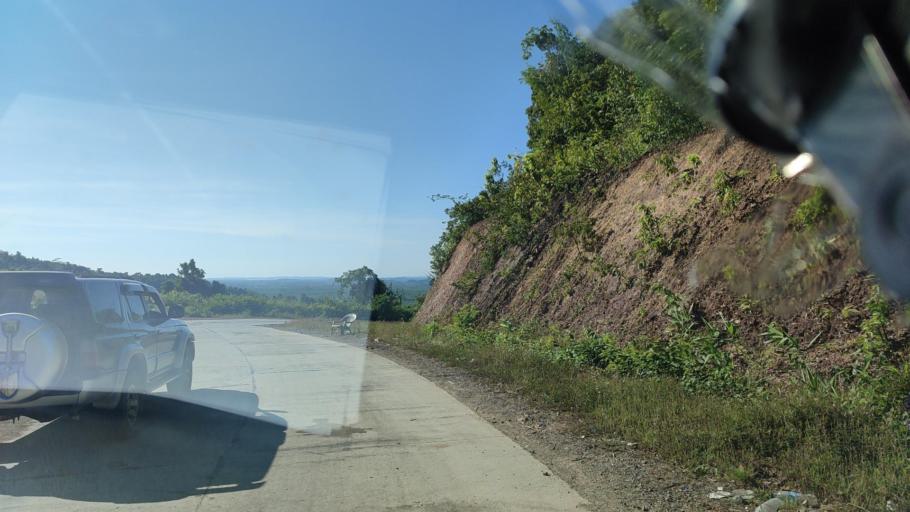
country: MM
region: Rakhine
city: Sittwe
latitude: 19.9316
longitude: 93.7643
